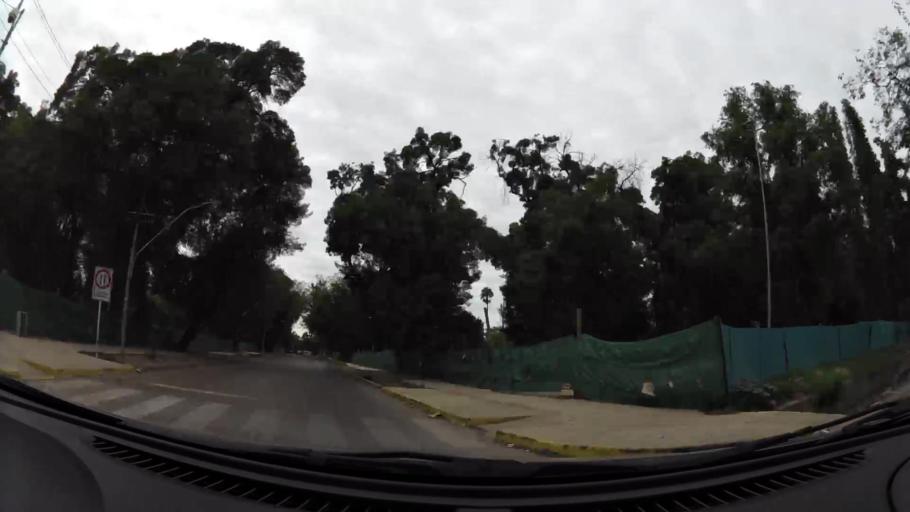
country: AR
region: Mendoza
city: Mendoza
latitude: -32.8828
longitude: -68.8296
